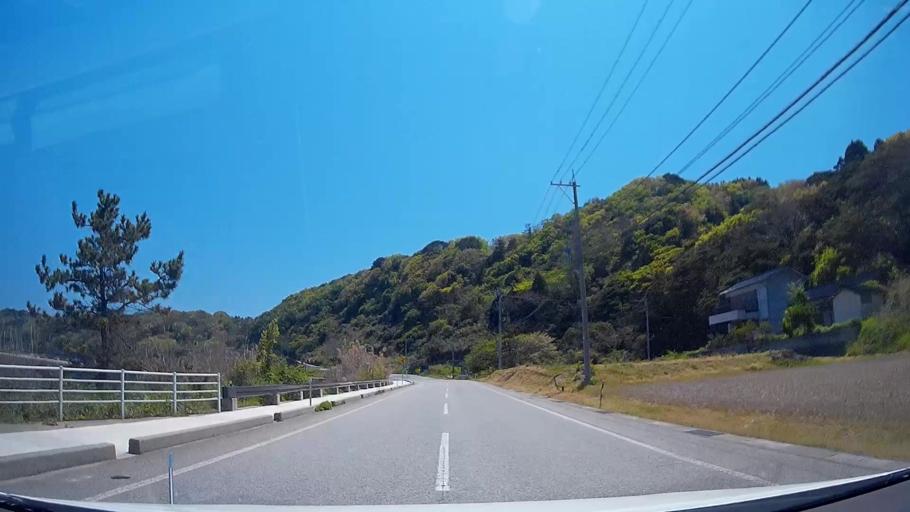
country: JP
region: Ishikawa
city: Nanao
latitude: 37.5266
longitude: 137.2944
